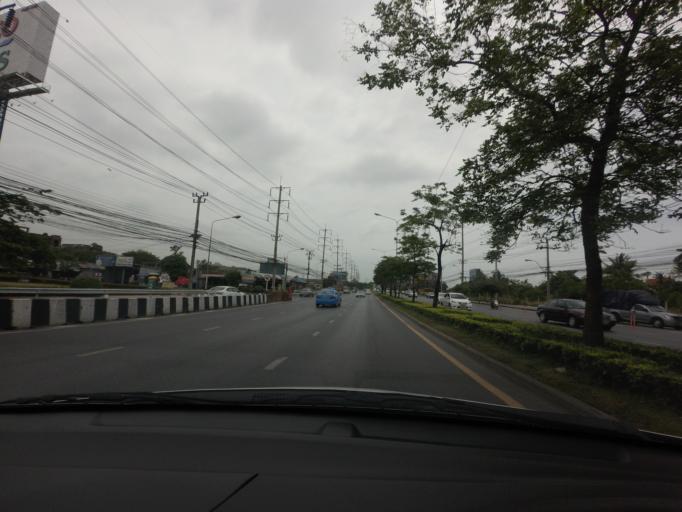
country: TH
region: Bangkok
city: Min Buri
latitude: 13.8186
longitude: 100.7280
